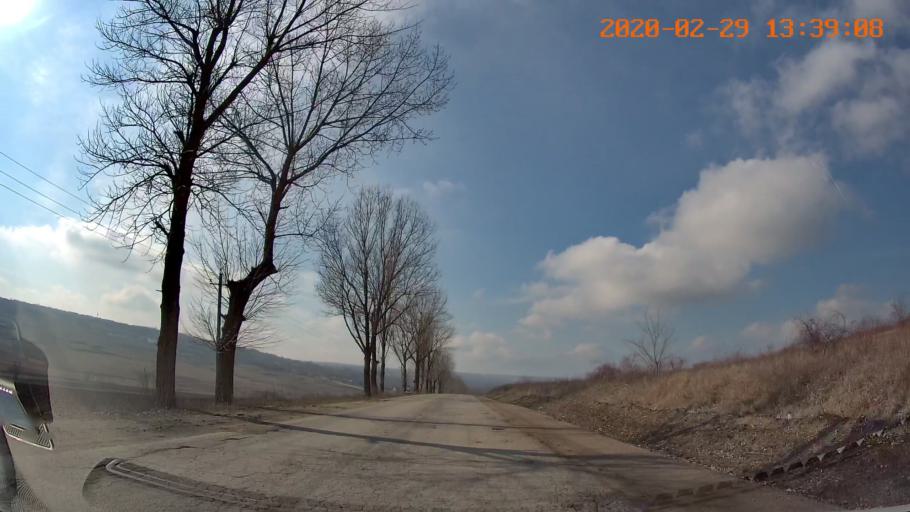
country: MD
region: Floresti
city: Leninskiy
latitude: 47.8514
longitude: 28.5863
